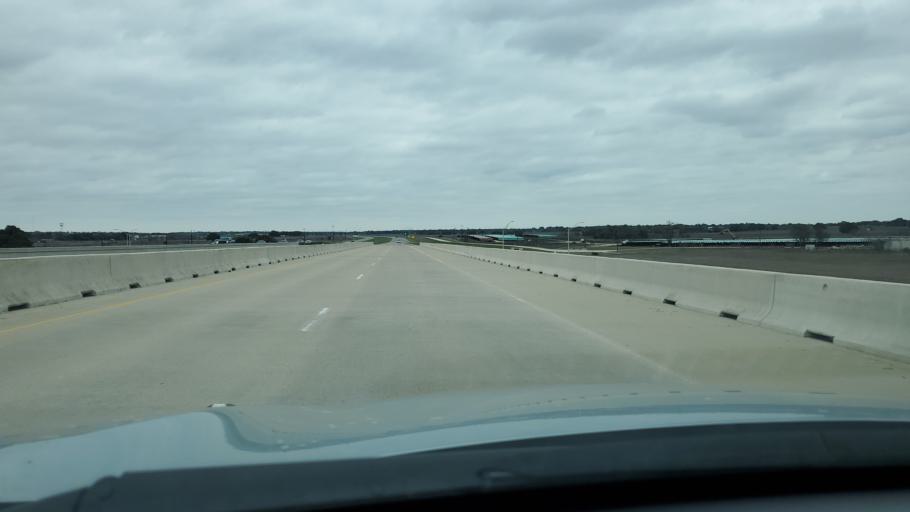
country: US
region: Texas
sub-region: Williamson County
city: Florence
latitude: 30.8259
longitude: -97.7815
